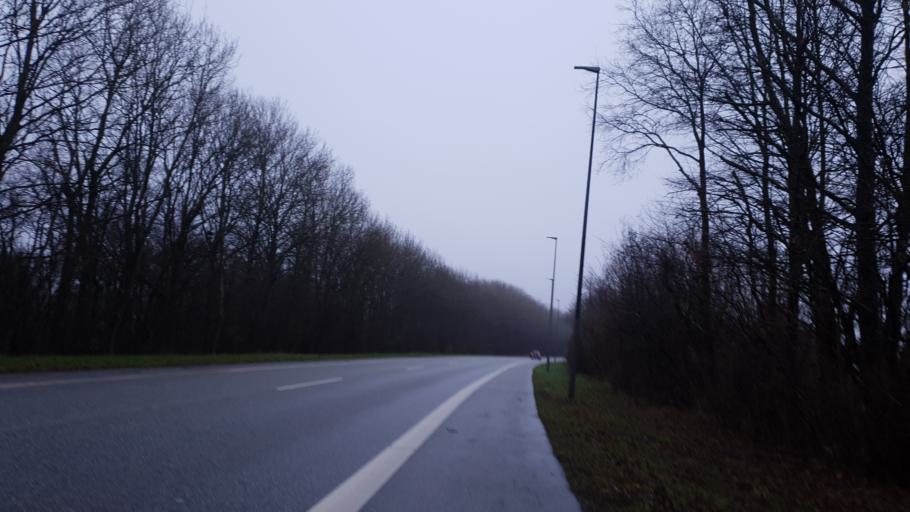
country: DK
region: Central Jutland
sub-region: Hedensted Kommune
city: Hedensted
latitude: 55.7874
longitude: 9.6995
